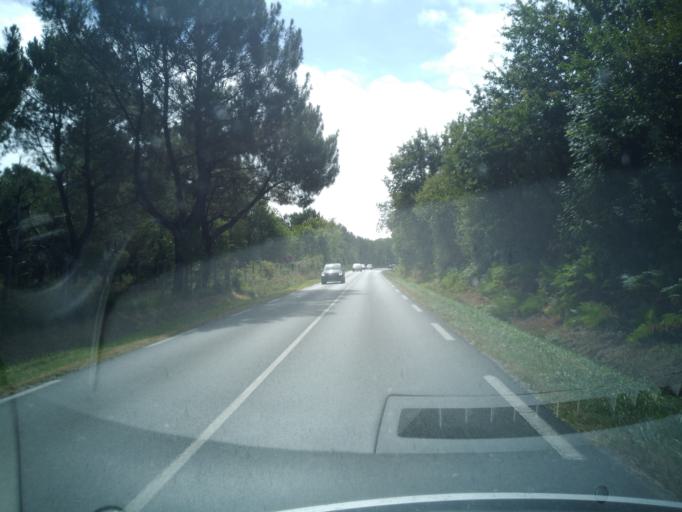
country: FR
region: Poitou-Charentes
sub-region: Departement de la Charente-Maritime
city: Chaillevette
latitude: 45.7180
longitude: -1.0720
